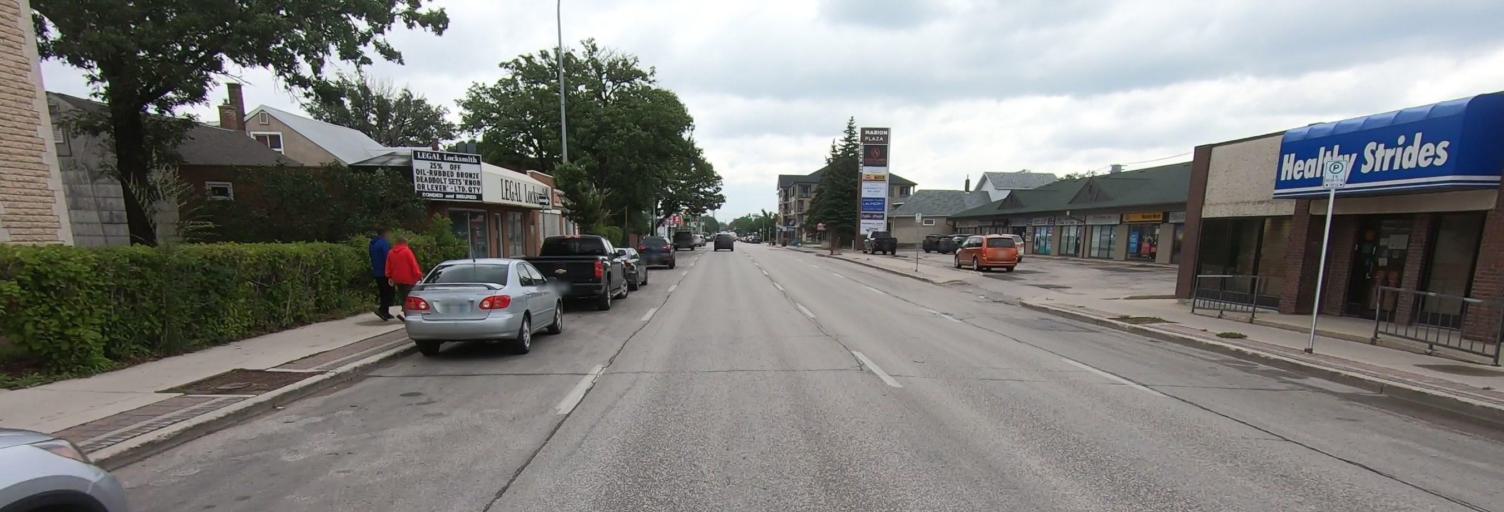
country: CA
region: Manitoba
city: Winnipeg
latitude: 49.8816
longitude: -97.1197
